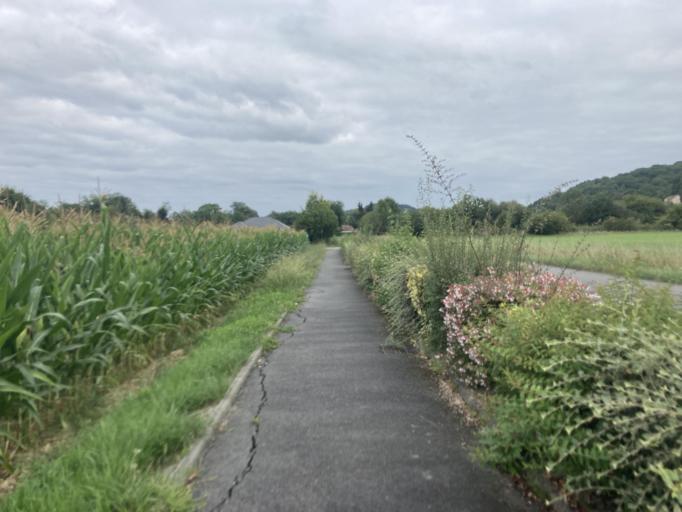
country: FR
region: Aquitaine
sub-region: Departement des Pyrenees-Atlantiques
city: Arbus
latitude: 43.3249
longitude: -0.4907
